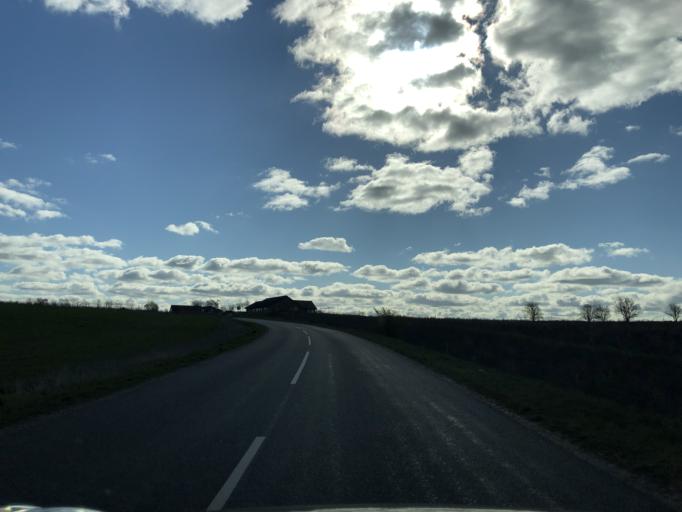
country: DK
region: North Denmark
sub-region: Vesthimmerland Kommune
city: Alestrup
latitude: 56.6074
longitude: 9.5425
